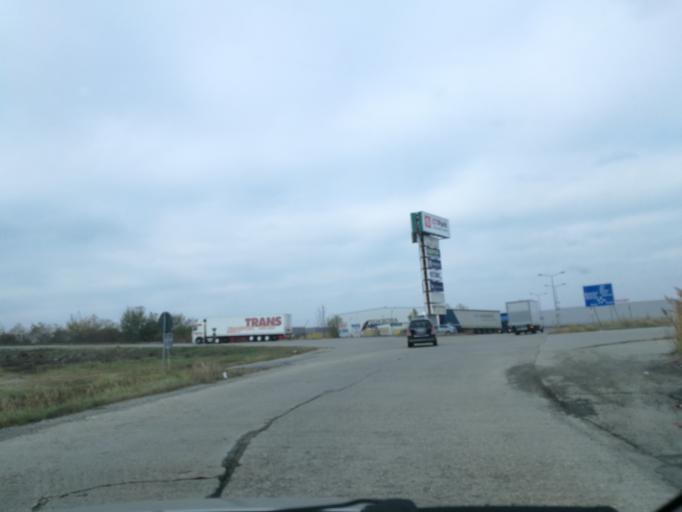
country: RO
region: Giurgiu
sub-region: Comuna Bolintin Deal
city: Bolintin Deal
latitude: 44.4673
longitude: 25.8279
